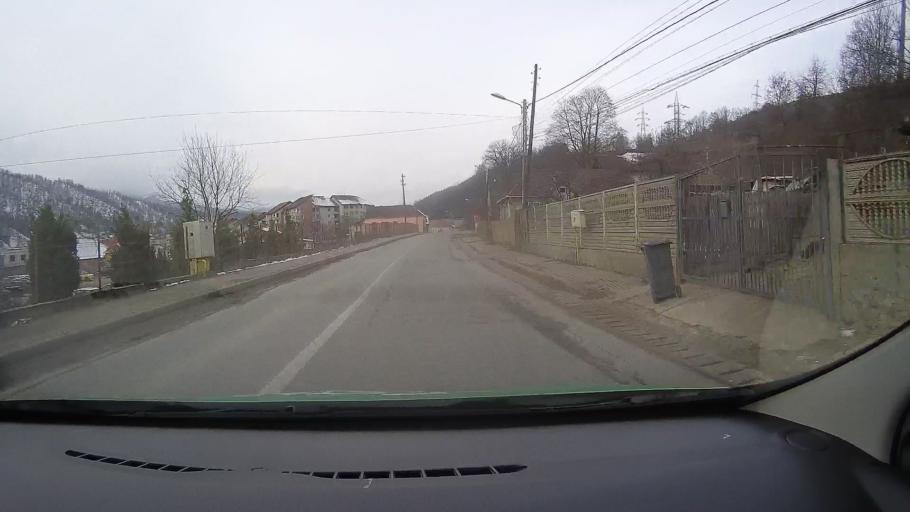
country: RO
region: Alba
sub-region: Oras Zlatna
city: Zlatna
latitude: 46.1077
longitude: 23.2326
